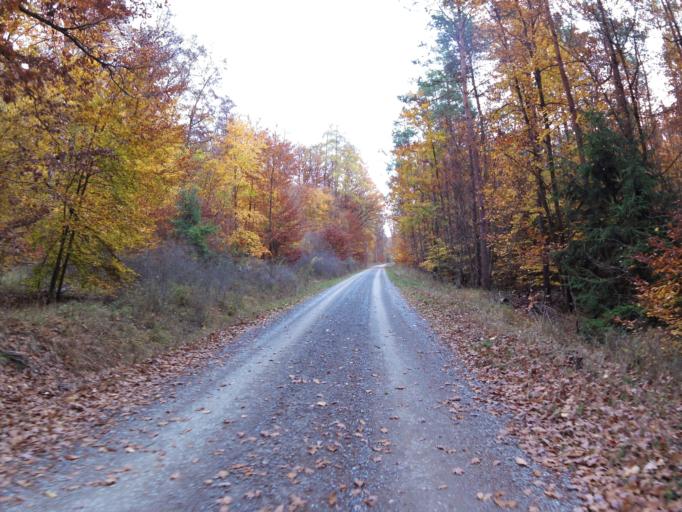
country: DE
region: Bavaria
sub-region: Regierungsbezirk Unterfranken
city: Kist
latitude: 49.7299
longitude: 9.8196
